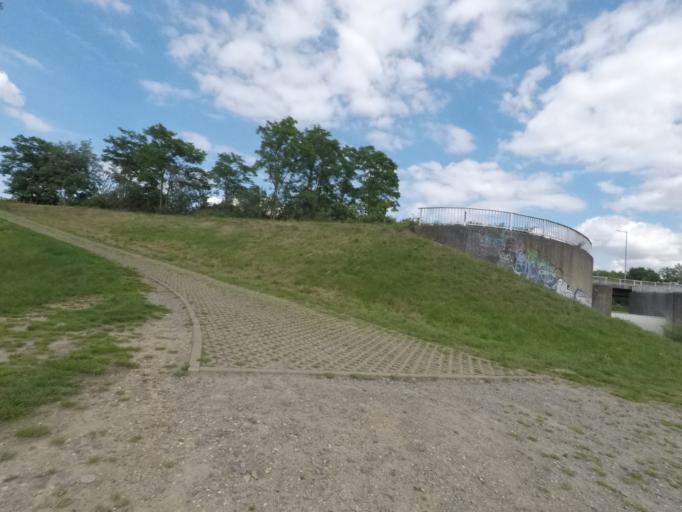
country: DE
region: North Rhine-Westphalia
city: Loehne
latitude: 52.1979
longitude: 8.7081
